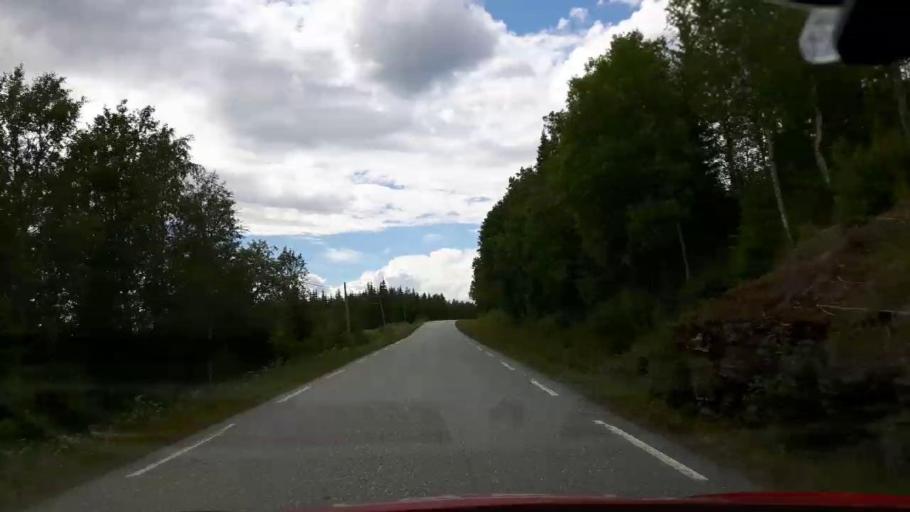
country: NO
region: Nord-Trondelag
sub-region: Lierne
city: Sandvika
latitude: 64.1177
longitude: 13.9536
